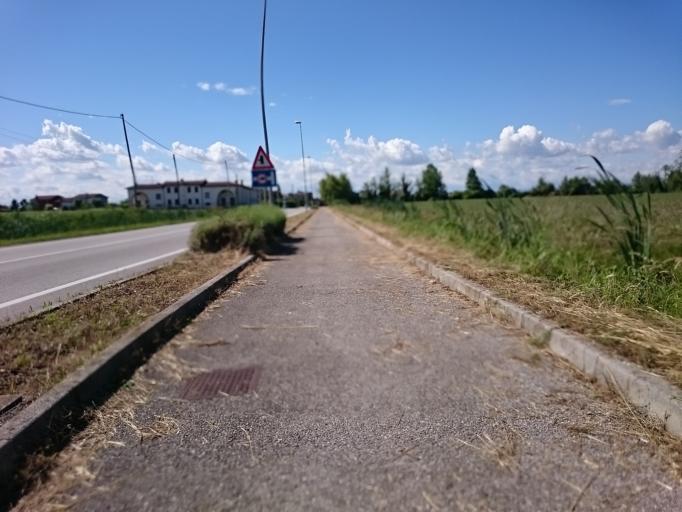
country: IT
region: Veneto
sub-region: Provincia di Venezia
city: Campolongo Maggiore Liettoli
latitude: 45.3282
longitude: 12.0237
